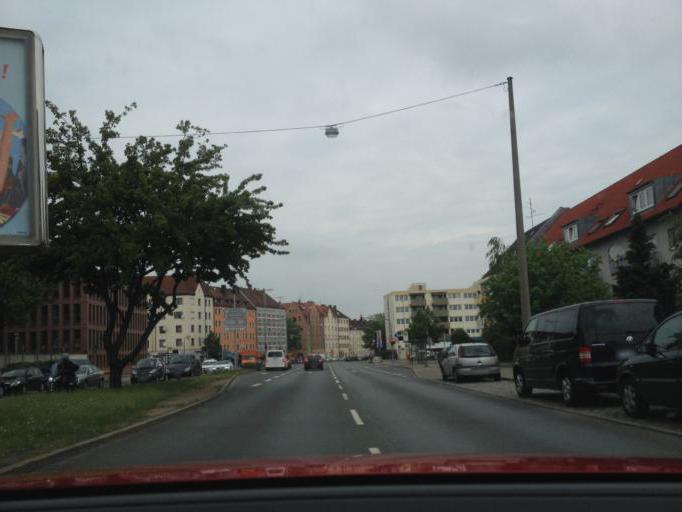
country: DE
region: Bavaria
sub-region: Regierungsbezirk Mittelfranken
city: Grossreuth bei Schweinau
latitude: 49.4380
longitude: 11.0372
